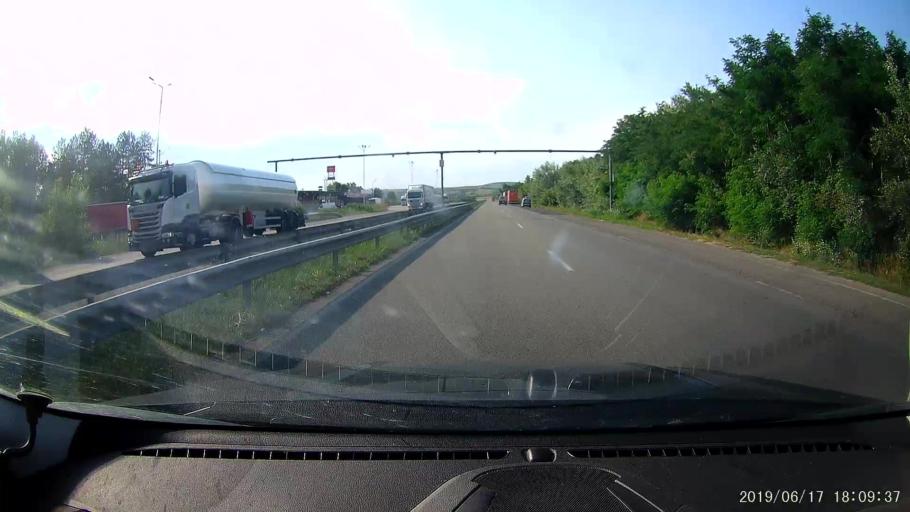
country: BG
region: Khaskovo
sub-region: Obshtina Lyubimets
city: Lyubimets
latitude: 41.8624
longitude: 26.0877
